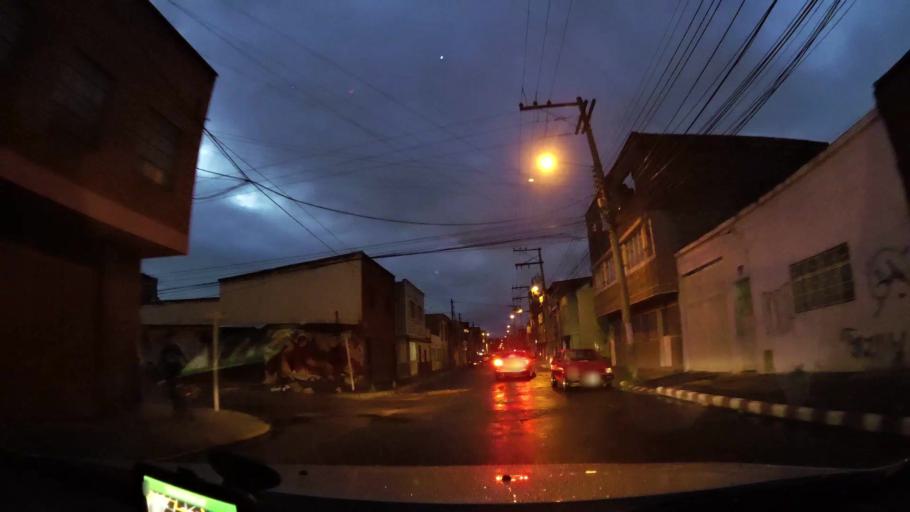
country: CO
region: Bogota D.C.
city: Bogota
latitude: 4.5813
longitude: -74.1291
